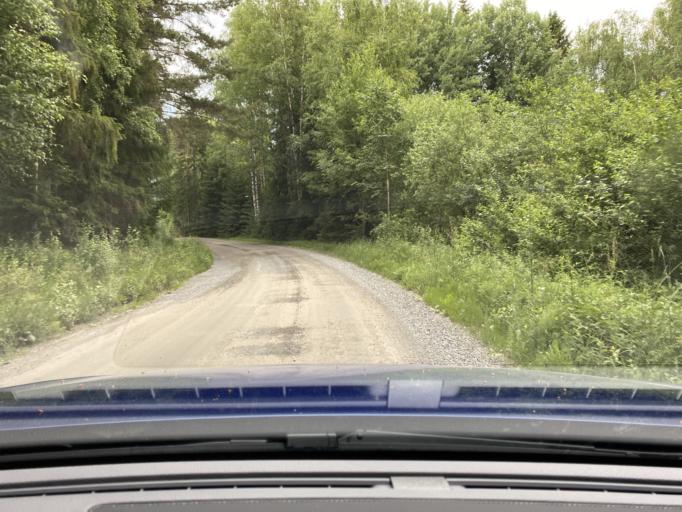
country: FI
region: Satakunta
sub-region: Rauma
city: Lappi
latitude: 61.1441
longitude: 21.9067
